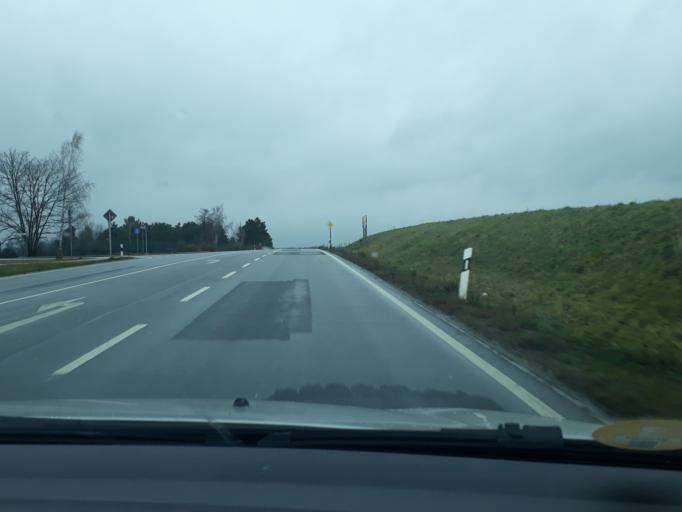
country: DE
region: Saxony
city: Bautzen
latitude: 51.2015
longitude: 14.4675
